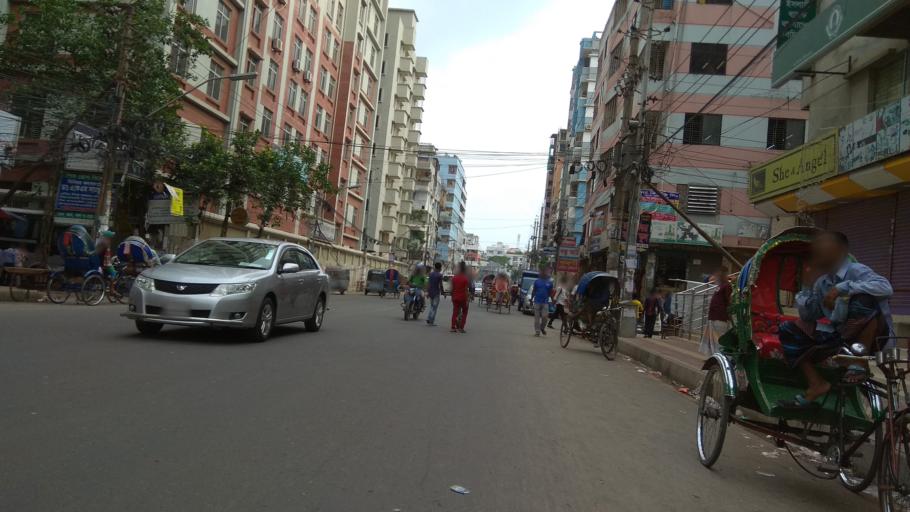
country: BD
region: Dhaka
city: Azimpur
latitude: 23.8123
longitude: 90.3567
